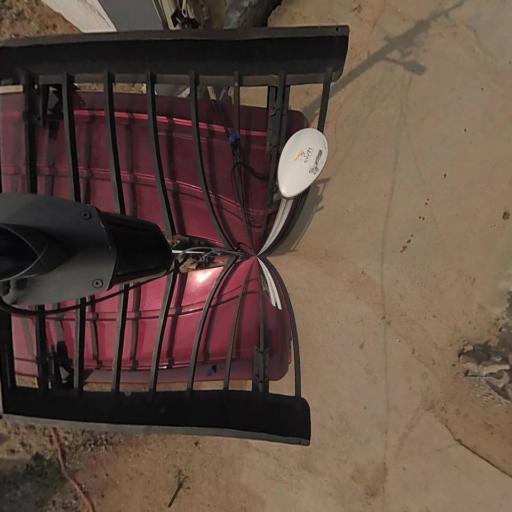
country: IN
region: Telangana
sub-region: Nalgonda
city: Nalgonda
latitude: 17.2091
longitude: 79.1574
